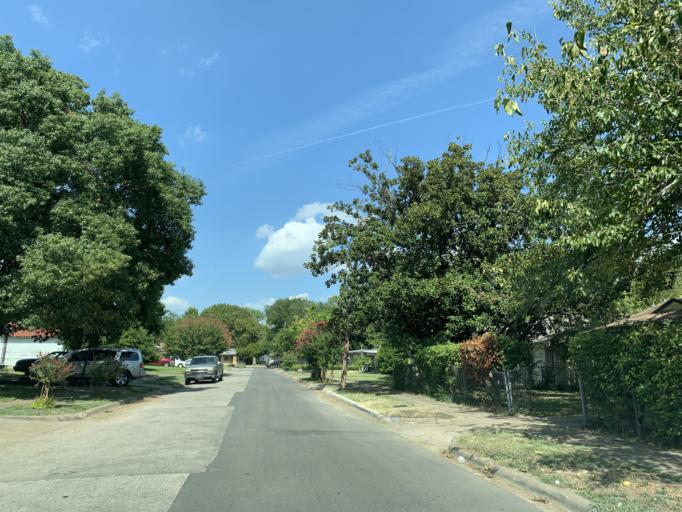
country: US
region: Texas
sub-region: Dallas County
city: Hutchins
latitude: 32.7033
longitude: -96.7693
